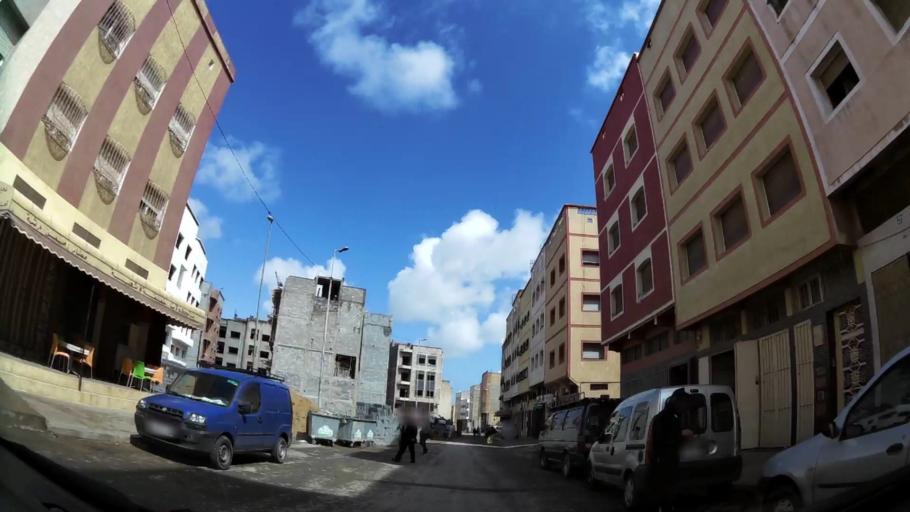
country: MA
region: Grand Casablanca
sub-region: Casablanca
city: Casablanca
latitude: 33.5366
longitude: -7.5786
